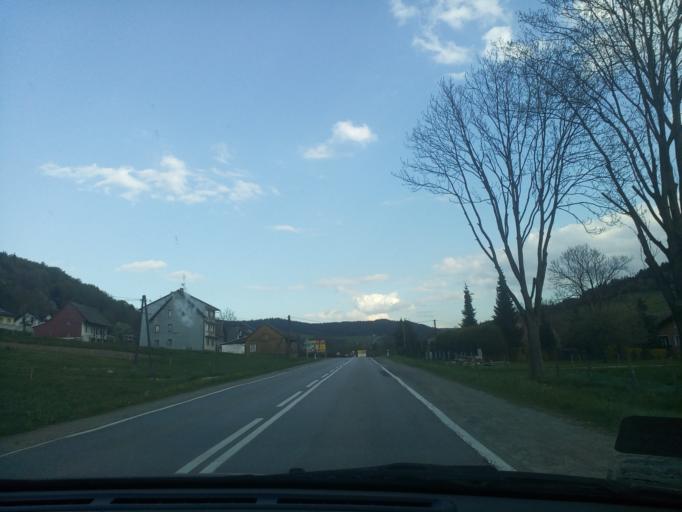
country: PL
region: Lesser Poland Voivodeship
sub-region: Powiat nowosadecki
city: Labowa
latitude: 49.5045
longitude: 20.8955
